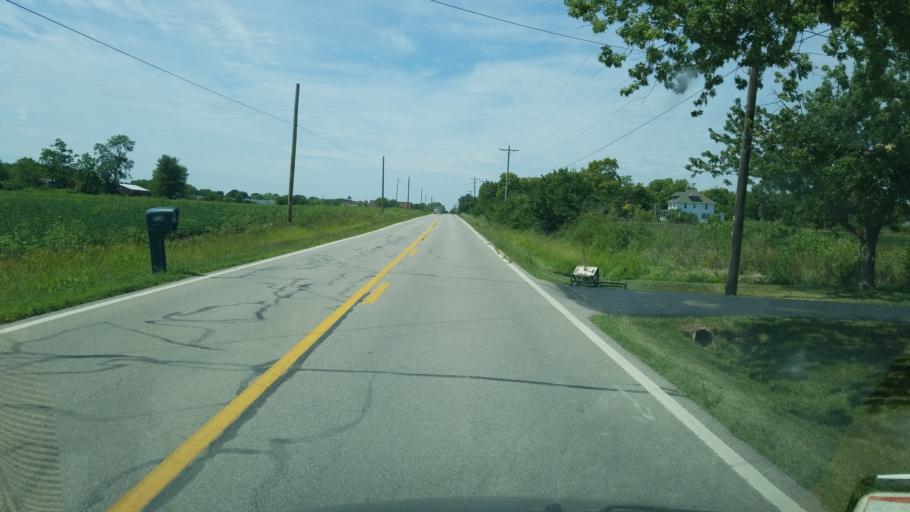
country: US
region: Ohio
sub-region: Franklin County
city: Grove City
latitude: 39.8753
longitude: -83.1766
